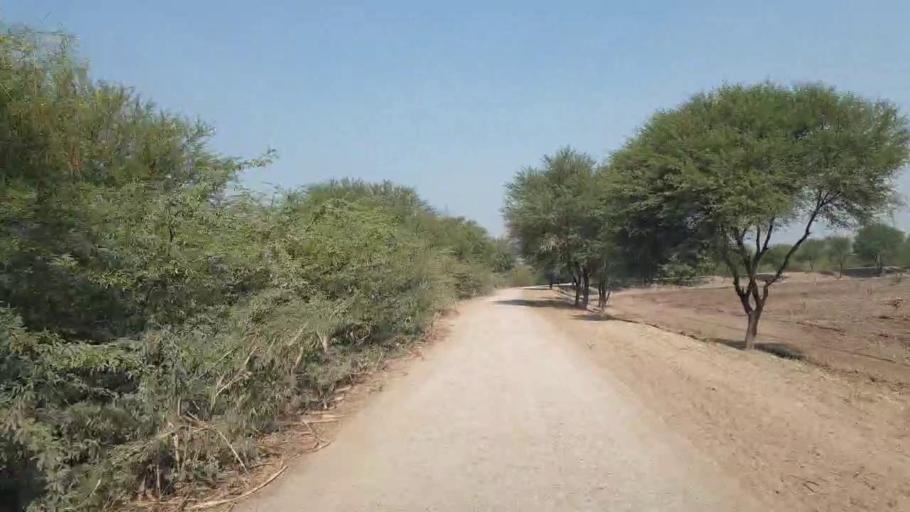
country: PK
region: Sindh
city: Chambar
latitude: 25.3507
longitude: 68.9156
